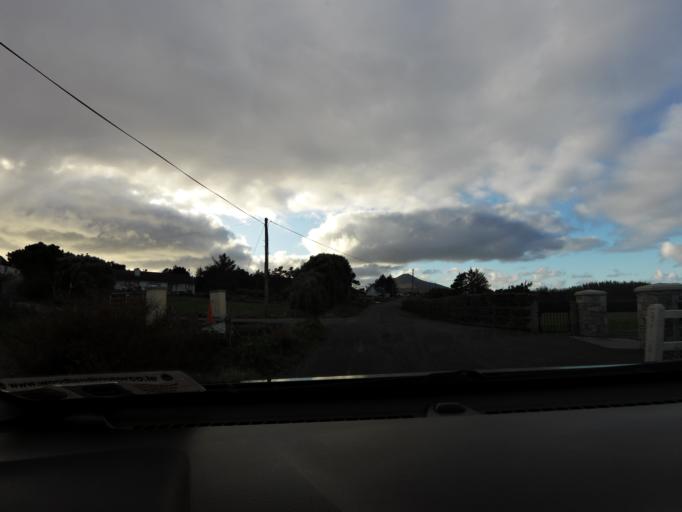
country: IE
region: Connaught
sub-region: Maigh Eo
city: Belmullet
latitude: 53.9952
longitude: -9.9451
